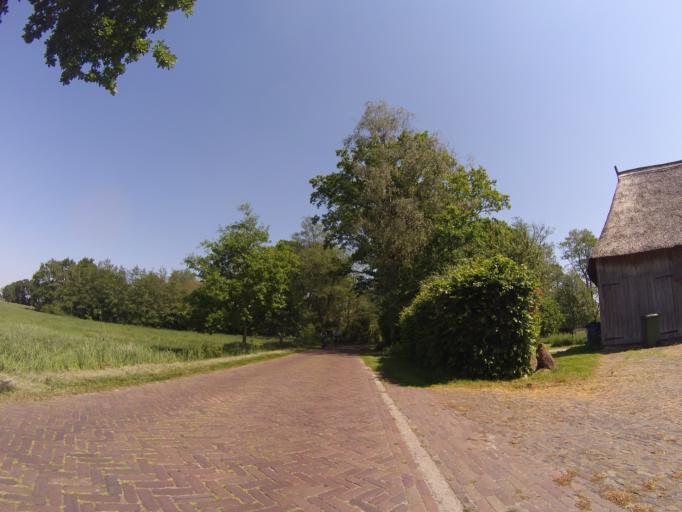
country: NL
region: Drenthe
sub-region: Gemeente Emmen
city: Schoonebeek
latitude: 52.6702
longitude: 6.8637
